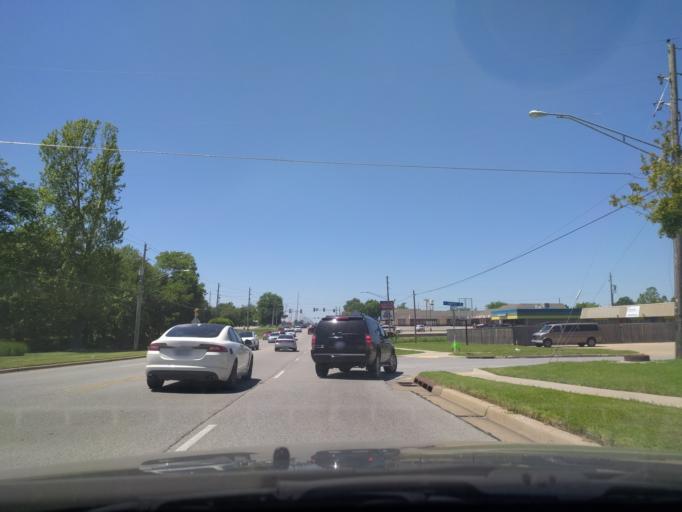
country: US
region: Oklahoma
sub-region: Tulsa County
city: Broken Arrow
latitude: 36.0610
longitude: -95.8071
